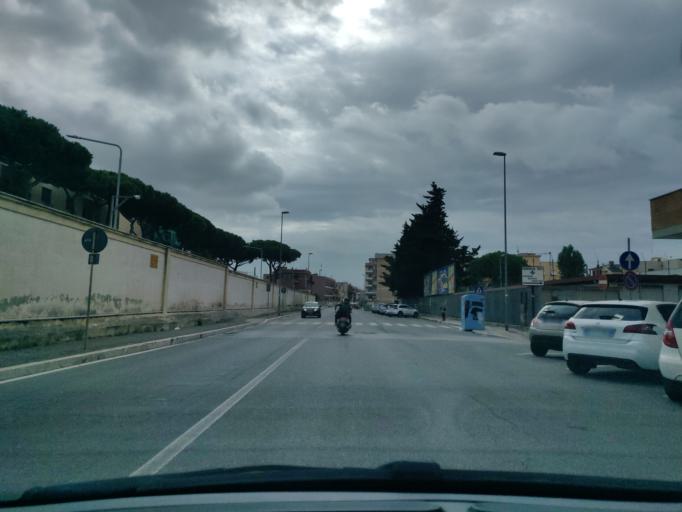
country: IT
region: Latium
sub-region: Citta metropolitana di Roma Capitale
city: Civitavecchia
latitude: 42.0978
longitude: 11.8012
